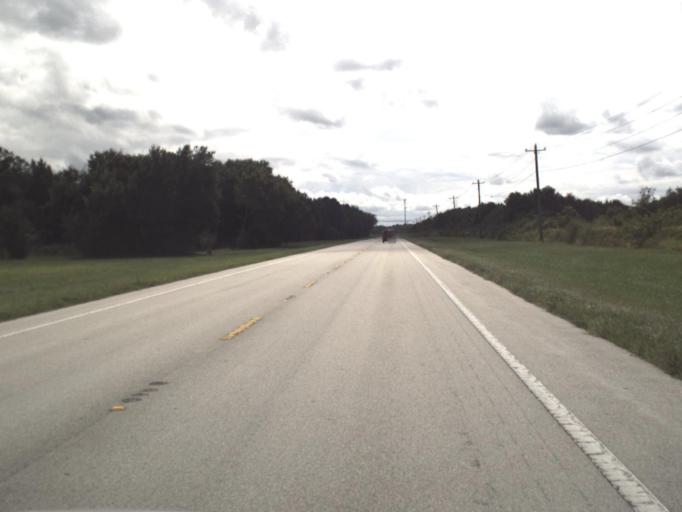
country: US
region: Florida
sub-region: Hillsborough County
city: Ruskin
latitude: 27.6096
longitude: -82.4166
